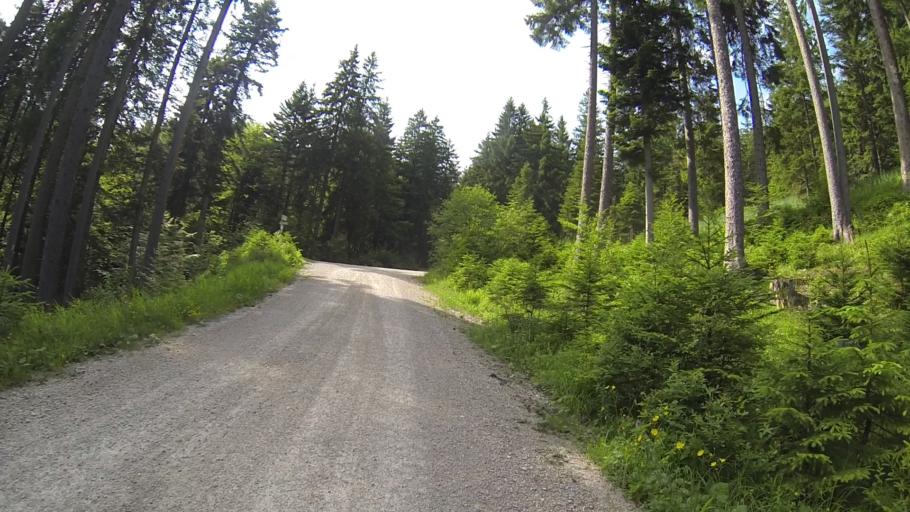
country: AT
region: Tyrol
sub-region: Politischer Bezirk Reutte
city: Jungholz
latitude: 47.5756
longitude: 10.4721
